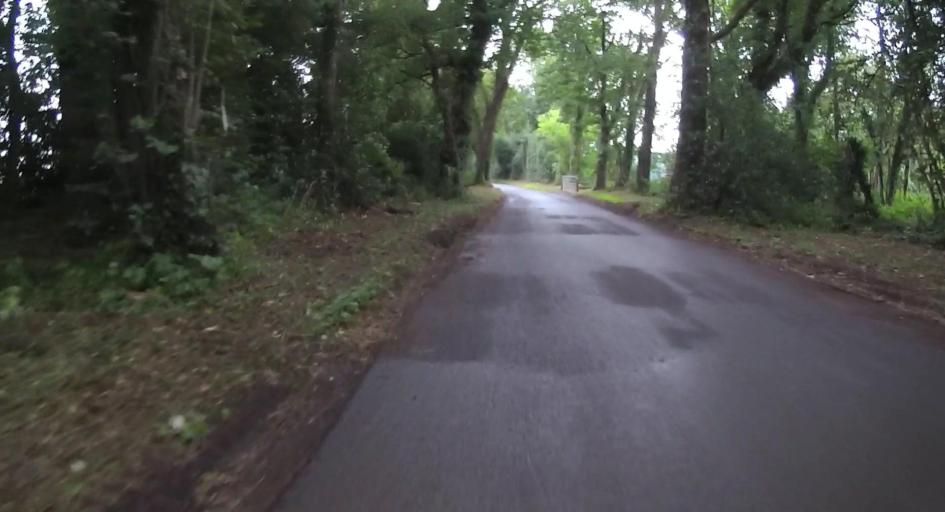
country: GB
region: England
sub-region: Hampshire
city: Andover
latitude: 51.1982
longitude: -1.4007
